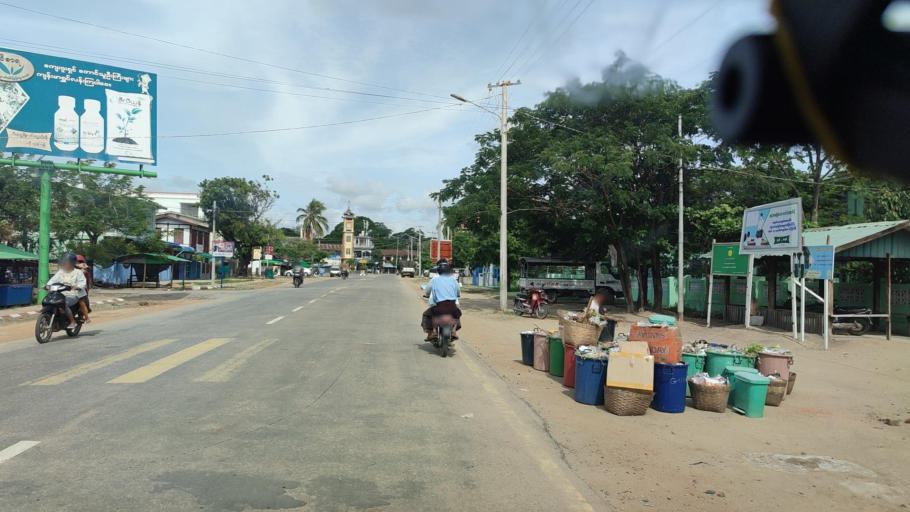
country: MM
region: Mandalay
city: Yamethin
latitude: 20.4305
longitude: 96.1406
